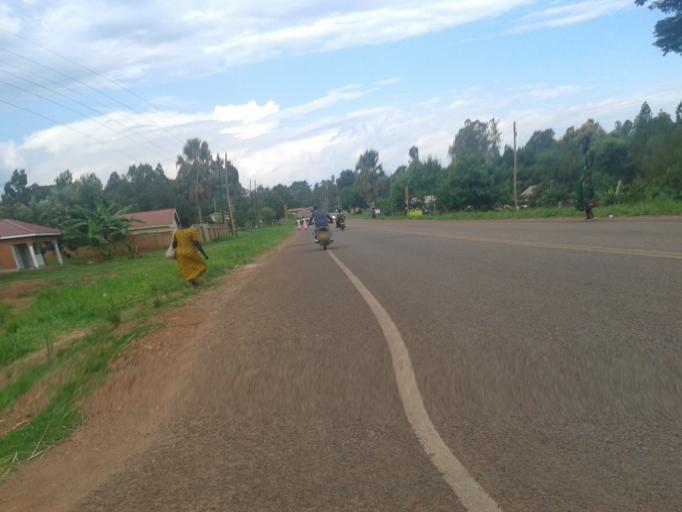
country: UG
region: Northern Region
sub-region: Gulu District
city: Gulu
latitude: 2.7622
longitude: 32.2755
